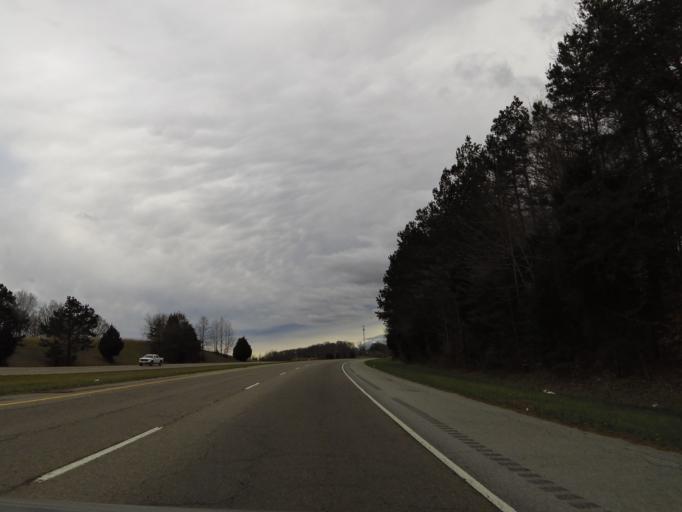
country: US
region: Tennessee
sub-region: Greene County
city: Tusculum
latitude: 36.2299
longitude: -82.6768
